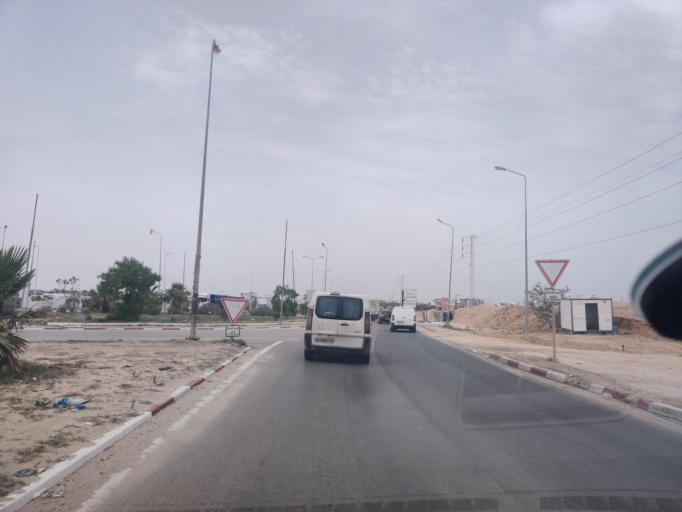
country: TN
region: Susah
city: Hammam Sousse
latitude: 35.8207
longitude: 10.5953
